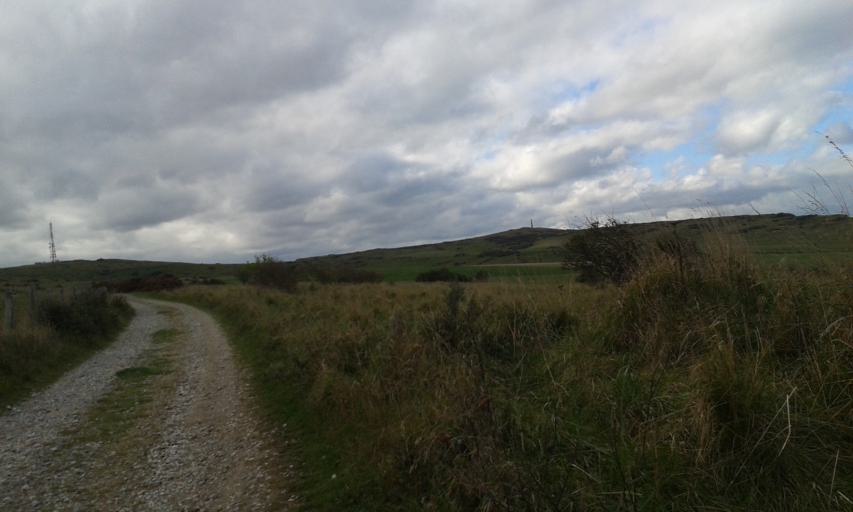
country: FR
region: Nord-Pas-de-Calais
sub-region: Departement du Pas-de-Calais
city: Sangatte
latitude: 50.9333
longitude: 1.7308
